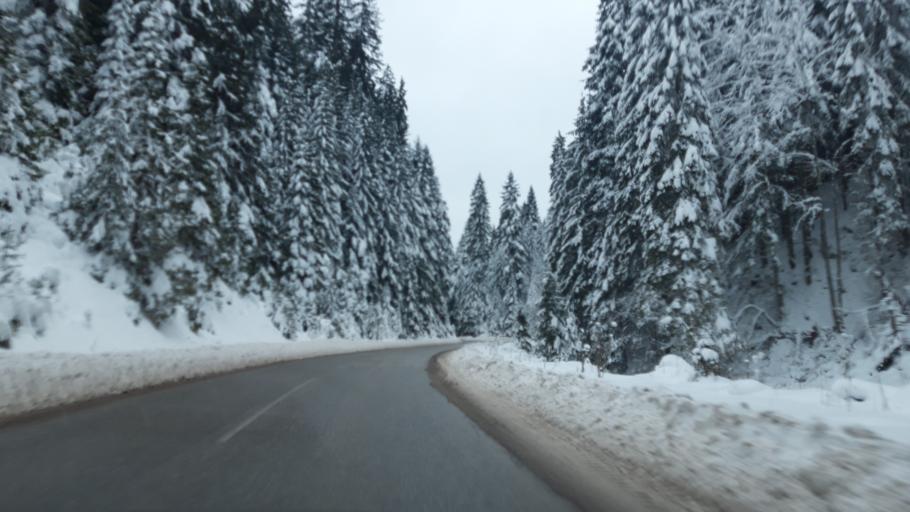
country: BA
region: Republika Srpska
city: Koran
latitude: 43.7646
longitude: 18.5469
